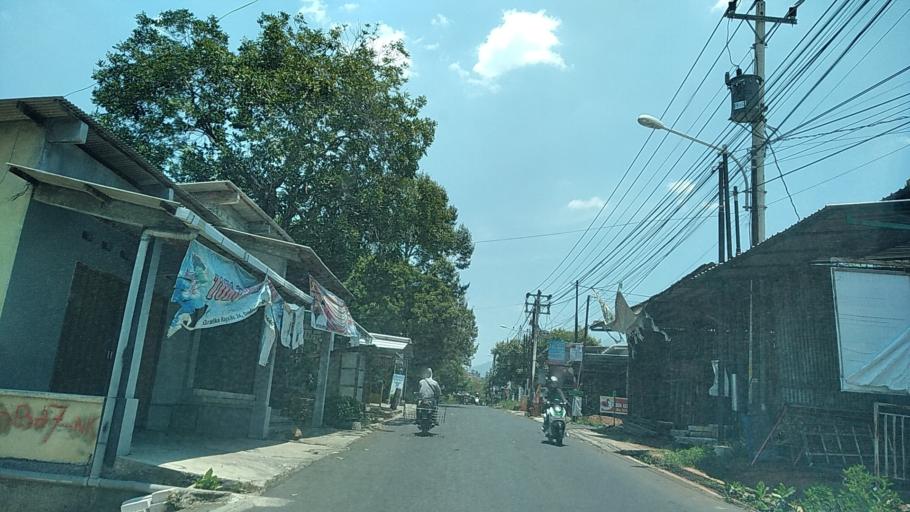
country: ID
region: Central Java
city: Ungaran
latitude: -7.0808
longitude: 110.4204
